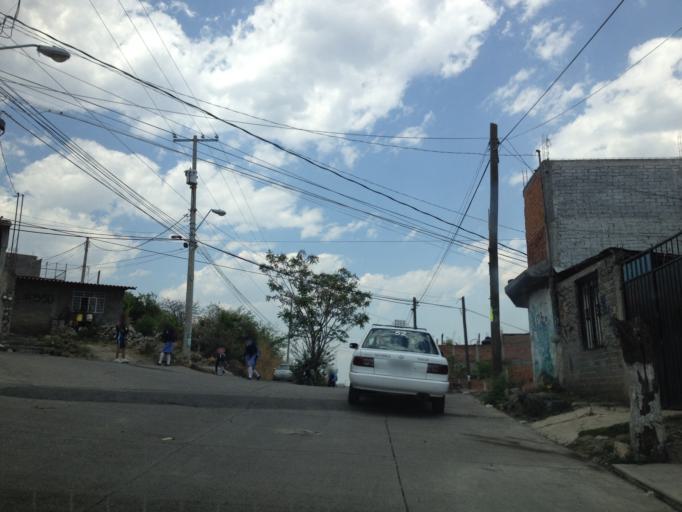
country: MX
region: Michoacan
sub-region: Morelia
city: San Antonio
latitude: 19.7048
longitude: -101.2464
